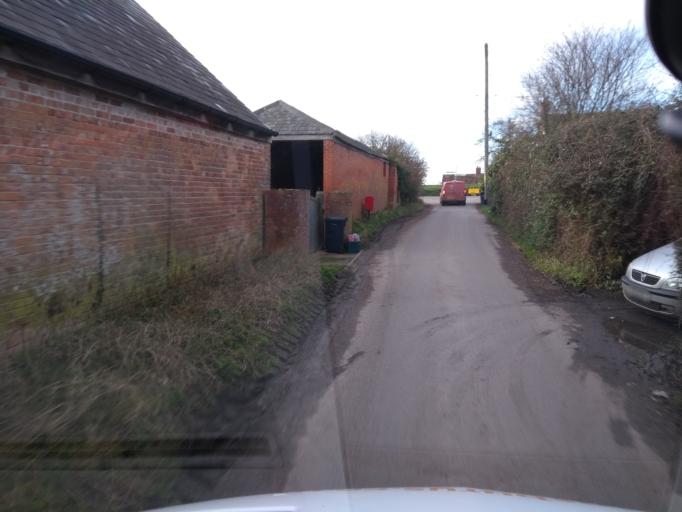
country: GB
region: England
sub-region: Somerset
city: Westonzoyland
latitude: 51.0749
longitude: -2.9258
